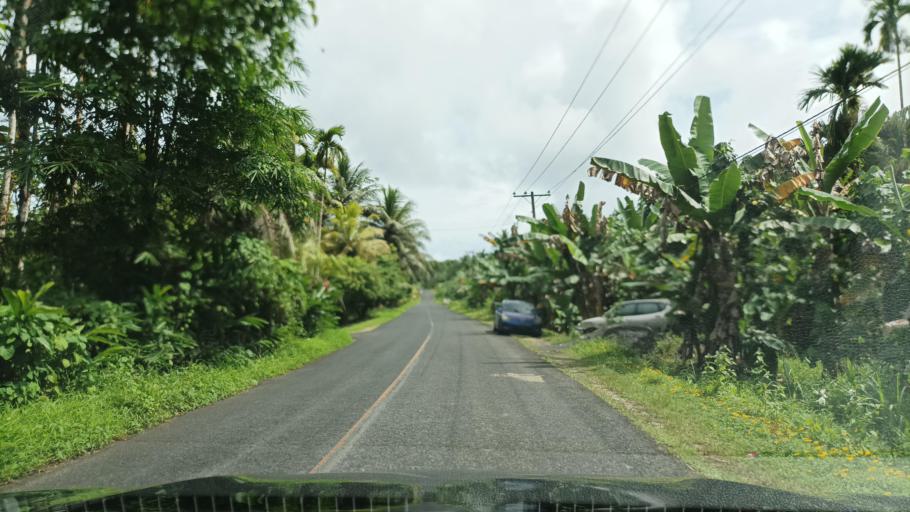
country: FM
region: Pohnpei
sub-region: Madolenihm Municipality
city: Madolenihm Municipality Government
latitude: 6.8850
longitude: 158.2899
